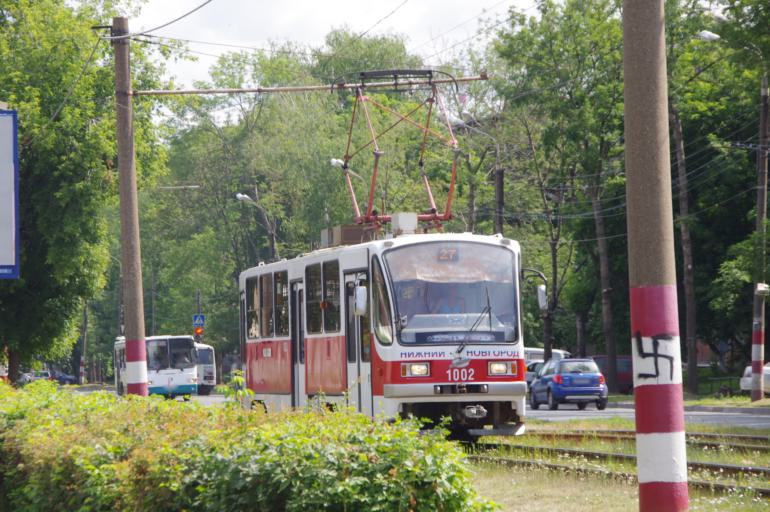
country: RU
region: Nizjnij Novgorod
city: Nizhniy Novgorod
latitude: 56.3010
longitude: 44.0345
